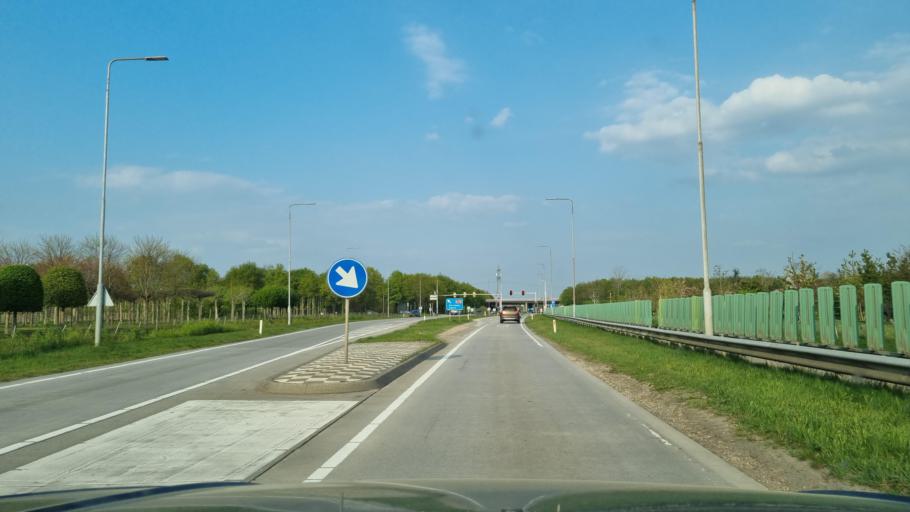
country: NL
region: North Brabant
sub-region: Gemeente Cuijk
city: Cuijk
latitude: 51.7293
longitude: 5.8447
